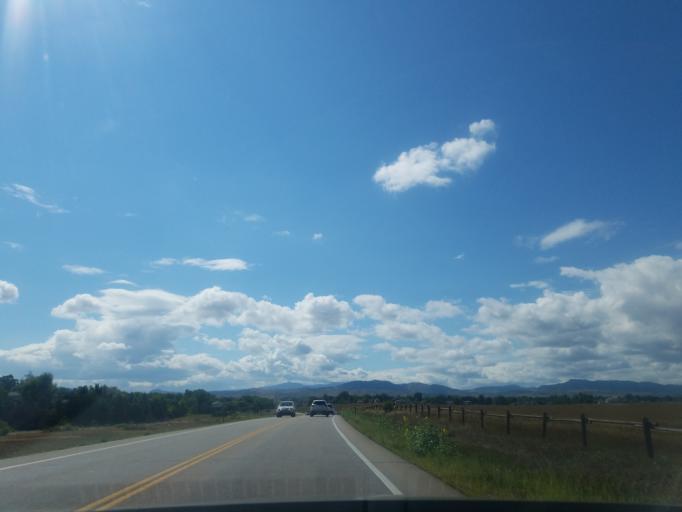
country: US
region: Colorado
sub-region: Larimer County
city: Loveland
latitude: 40.4801
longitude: -105.0601
